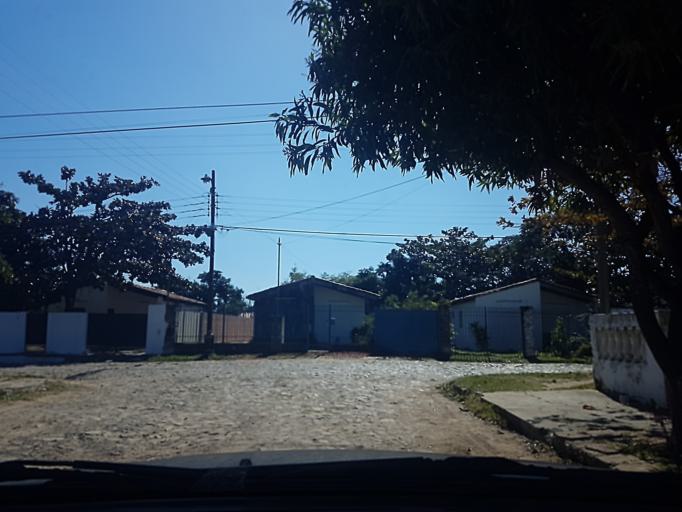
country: PY
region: Central
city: Colonia Mariano Roque Alonso
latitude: -25.2128
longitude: -57.5389
